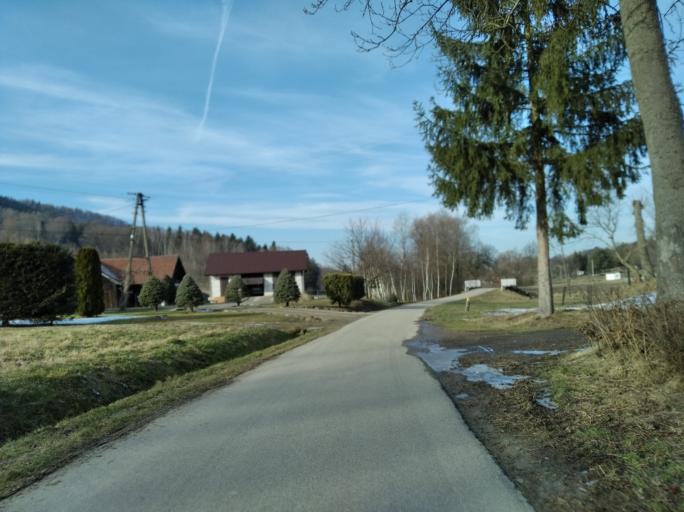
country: PL
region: Subcarpathian Voivodeship
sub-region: Powiat krosnienski
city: Odrzykon
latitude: 49.7807
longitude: 21.7620
